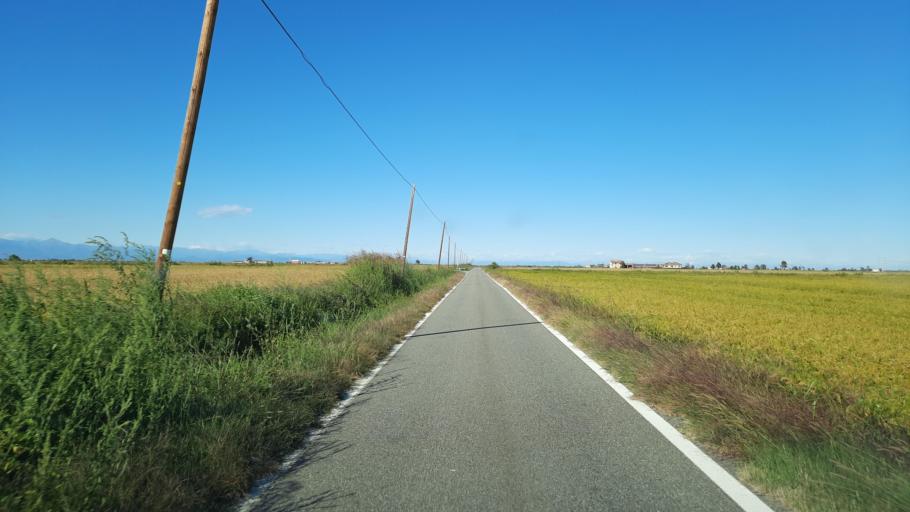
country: IT
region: Piedmont
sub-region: Provincia di Vercelli
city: Ronsecco
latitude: 45.2584
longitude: 8.2829
